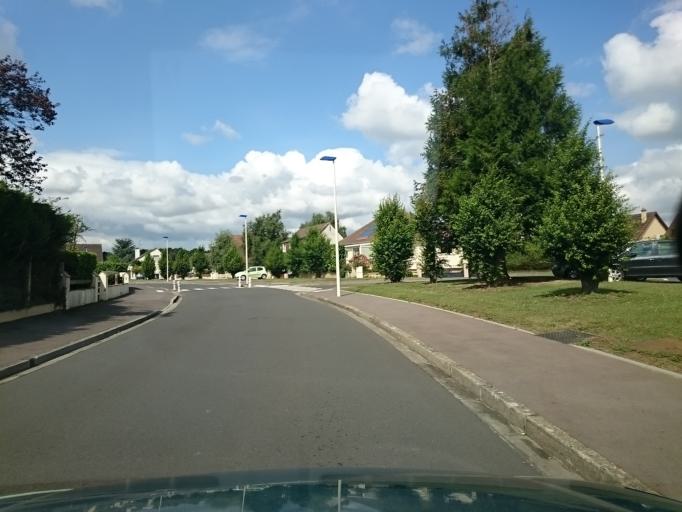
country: FR
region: Lower Normandy
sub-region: Departement du Calvados
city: Ifs
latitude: 49.1442
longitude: -0.3523
